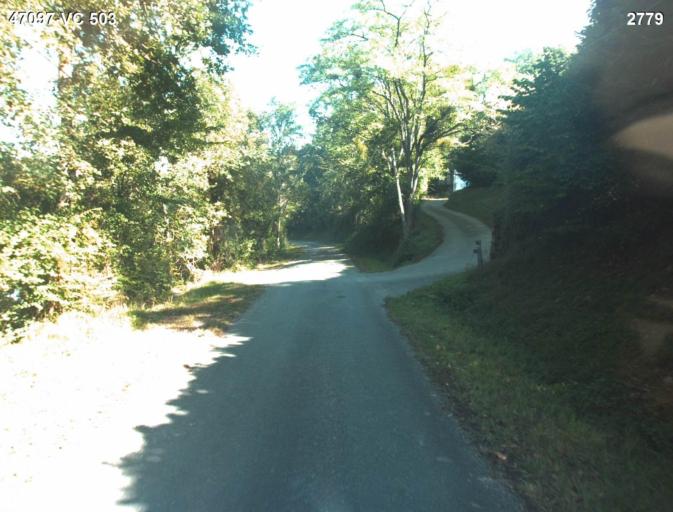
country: FR
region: Aquitaine
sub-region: Departement du Lot-et-Garonne
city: Port-Sainte-Marie
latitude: 44.2139
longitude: 0.3710
